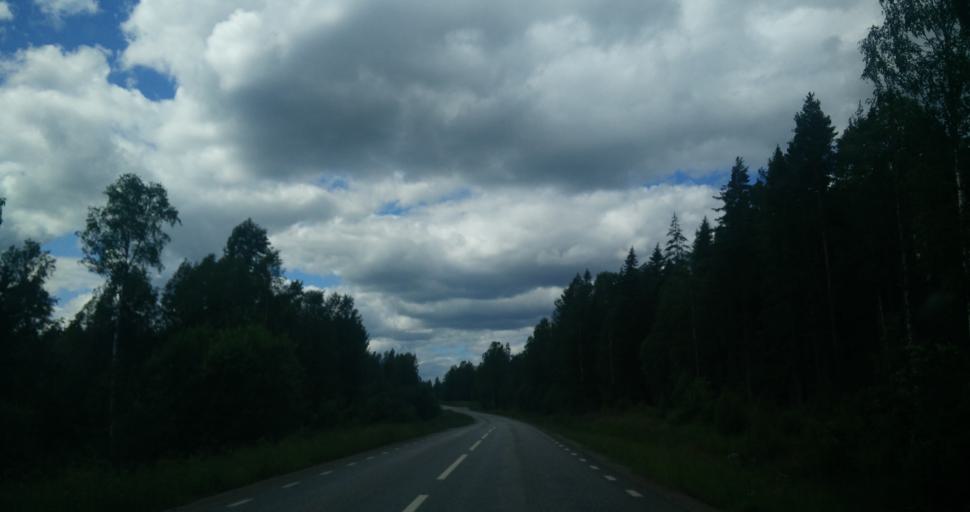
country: SE
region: Gaevleborg
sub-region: Nordanstigs Kommun
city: Bergsjoe
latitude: 62.0837
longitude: 16.8028
